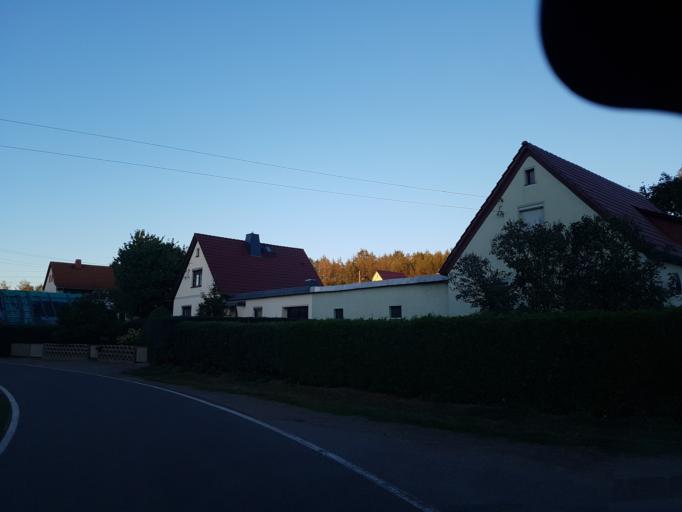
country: DE
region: Saxony
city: Naundorf
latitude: 51.2795
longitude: 13.1495
